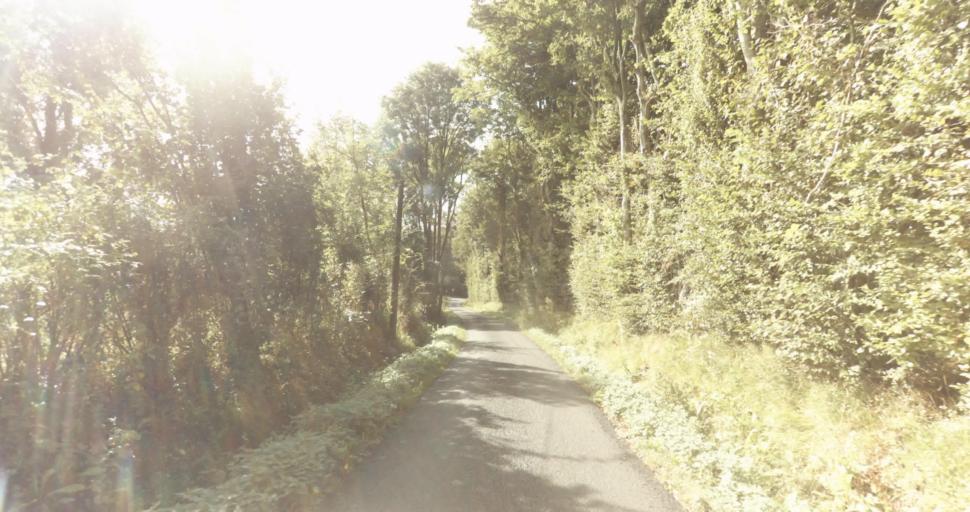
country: FR
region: Lower Normandy
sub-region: Departement de l'Orne
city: Vimoutiers
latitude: 48.8704
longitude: 0.1680
